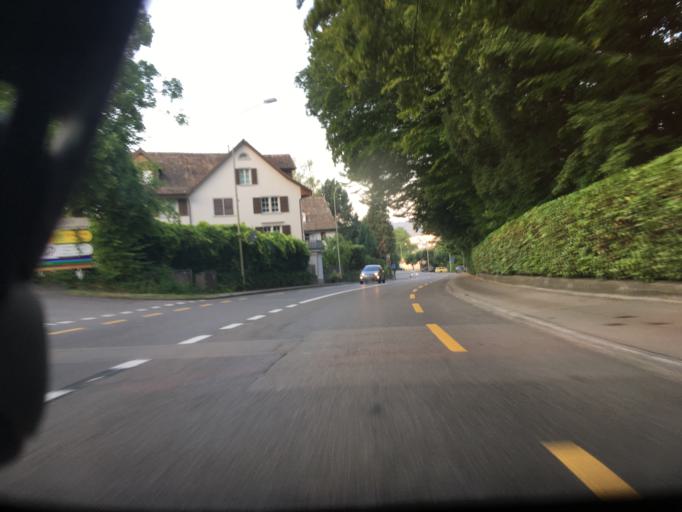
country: CH
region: Zurich
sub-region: Bezirk Meilen
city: Erlenbach / links des Dorfbachs oberhalb Bahnlinie
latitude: 47.2965
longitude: 8.5985
